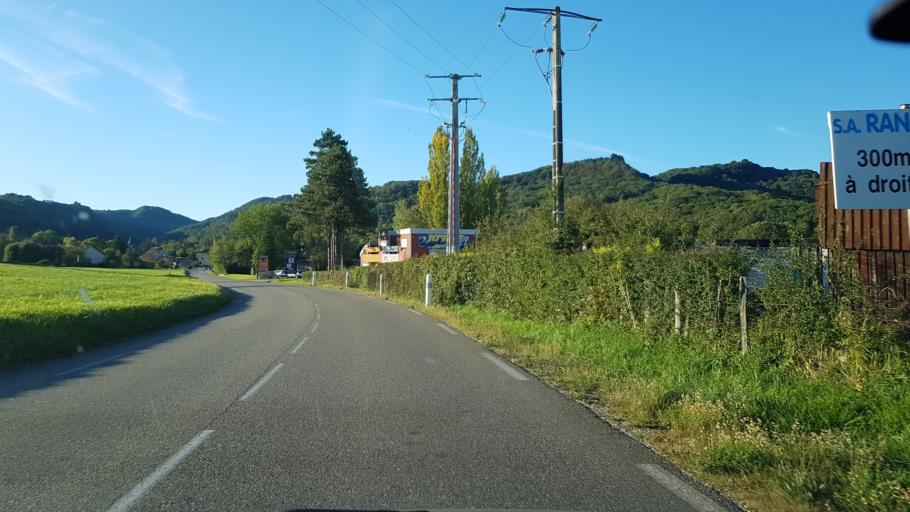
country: FR
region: Franche-Comte
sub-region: Departement du Jura
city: Lons-le-Saunier
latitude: 46.6528
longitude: 5.5378
